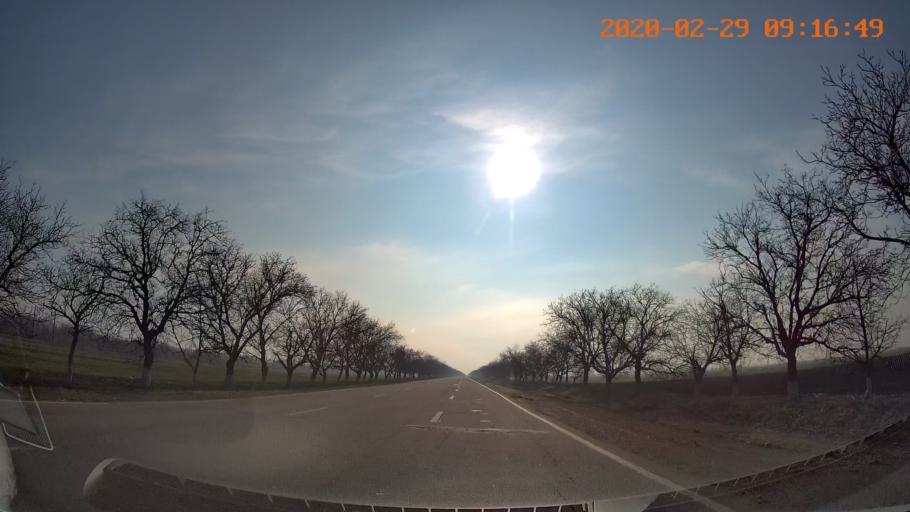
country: MD
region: Telenesti
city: Pervomaisc
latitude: 46.7884
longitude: 29.8933
